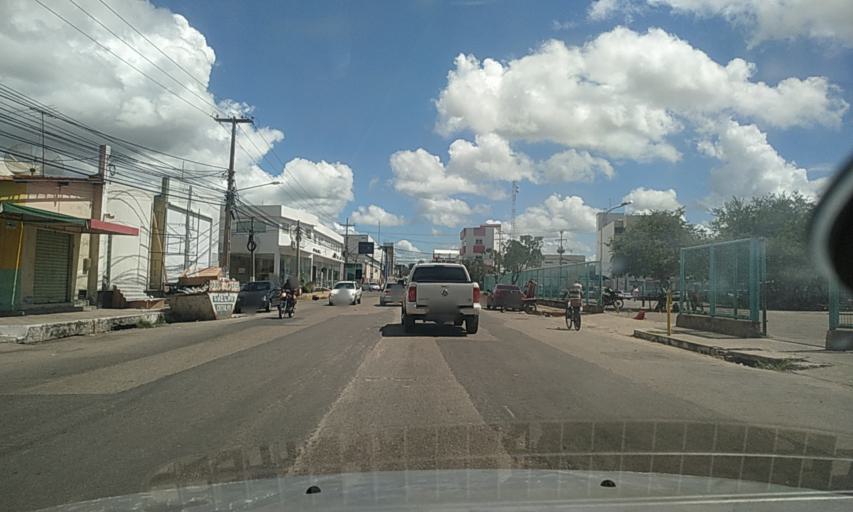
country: BR
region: Rio Grande do Norte
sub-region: Mossoro
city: Mossoro
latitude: -5.1896
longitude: -37.3375
